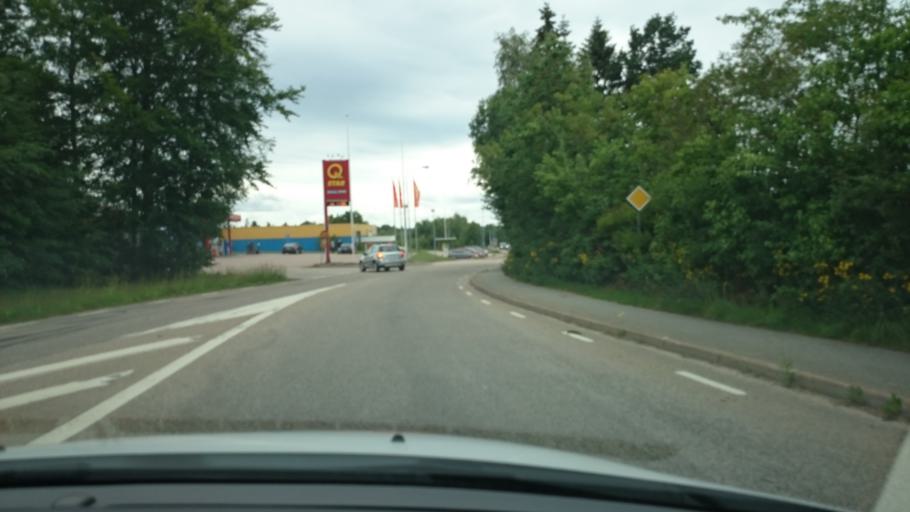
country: SE
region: Halland
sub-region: Hylte Kommun
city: Hyltebruk
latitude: 56.9884
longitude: 13.2381
